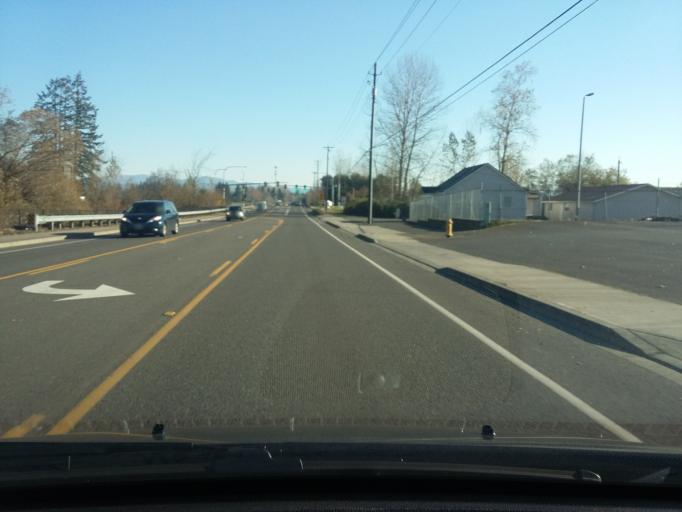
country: US
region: Washington
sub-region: Clark County
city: Barberton
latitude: 45.6860
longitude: -122.6111
